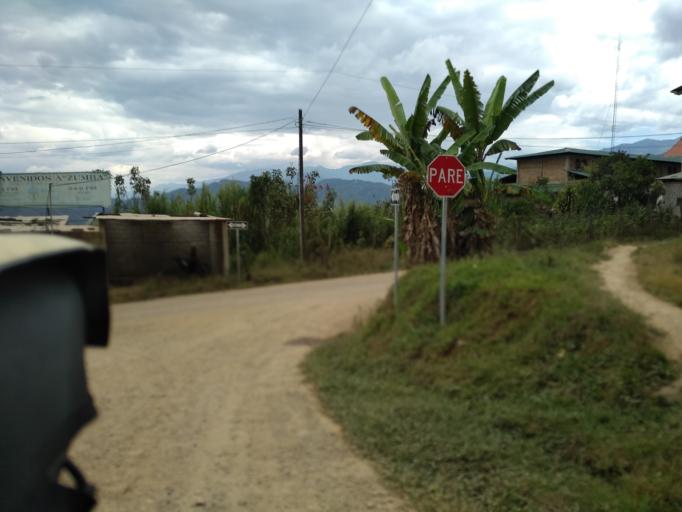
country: PE
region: Cajamarca
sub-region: Provincia de San Ignacio
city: Namballe
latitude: -4.8630
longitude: -79.1298
